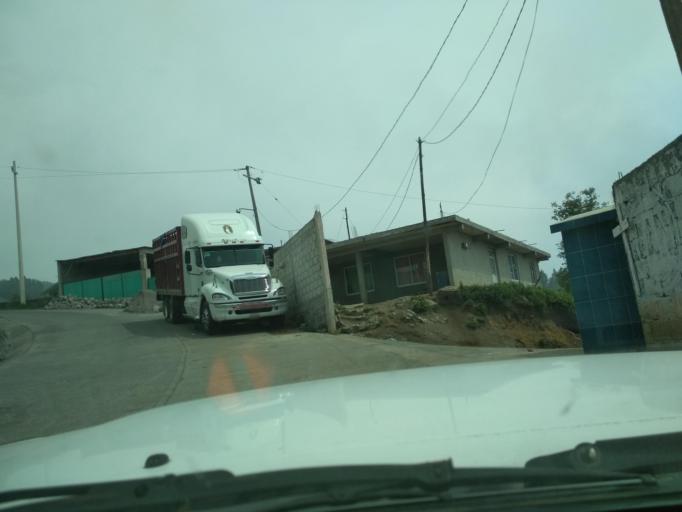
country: MX
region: Veracruz
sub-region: Mariano Escobedo
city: San Isidro el Berro
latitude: 18.9763
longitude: -97.2054
